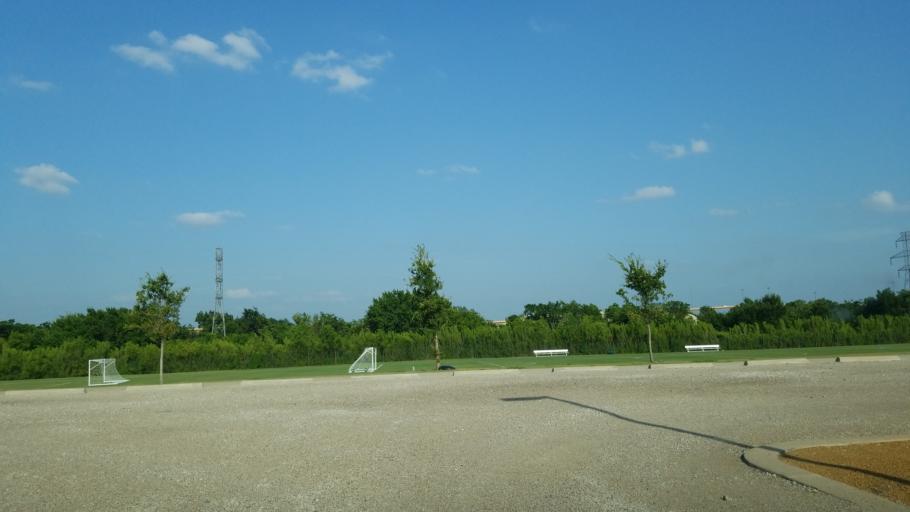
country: US
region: Texas
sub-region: Dallas County
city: Farmers Branch
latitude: 32.8786
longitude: -96.9050
